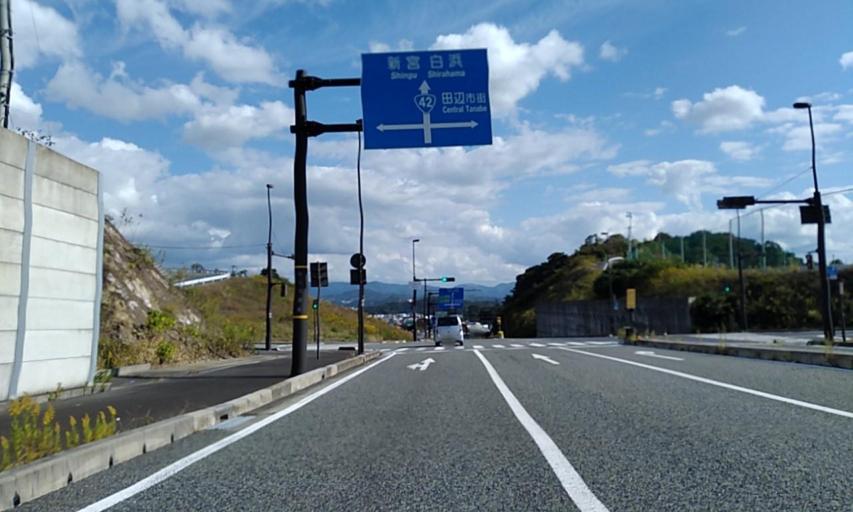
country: JP
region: Wakayama
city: Tanabe
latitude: 33.7472
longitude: 135.3656
